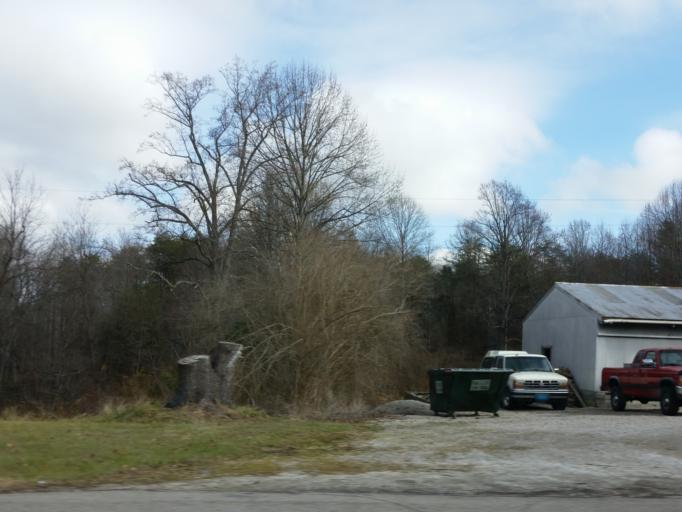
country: US
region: Indiana
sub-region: Jennings County
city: North Vernon
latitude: 38.9245
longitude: -85.5558
